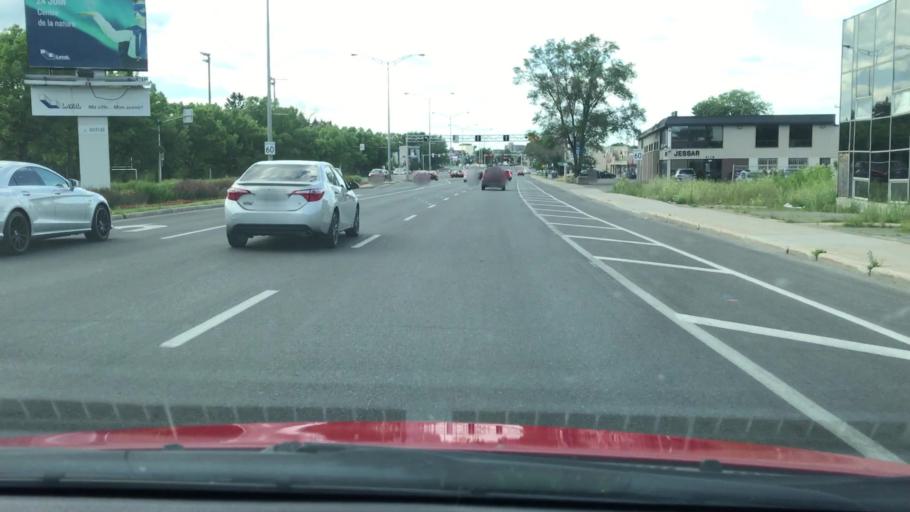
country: CA
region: Quebec
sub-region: Laval
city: Laval
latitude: 45.5346
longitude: -73.7298
